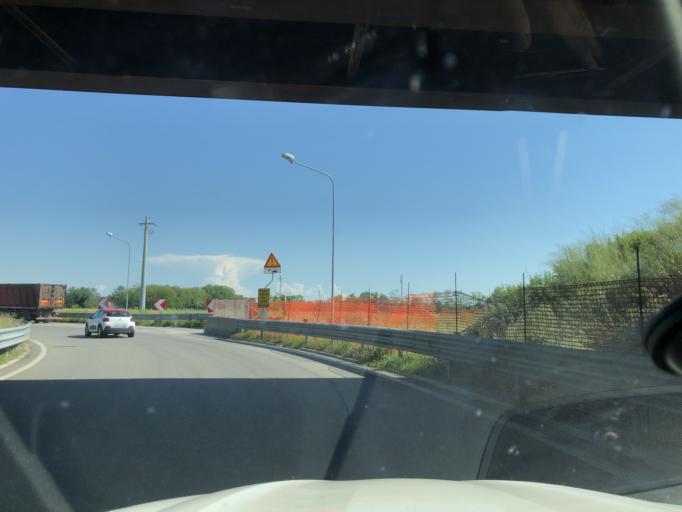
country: IT
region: Lombardy
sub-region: Citta metropolitana di Milano
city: Passirana
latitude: 45.5547
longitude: 9.0391
